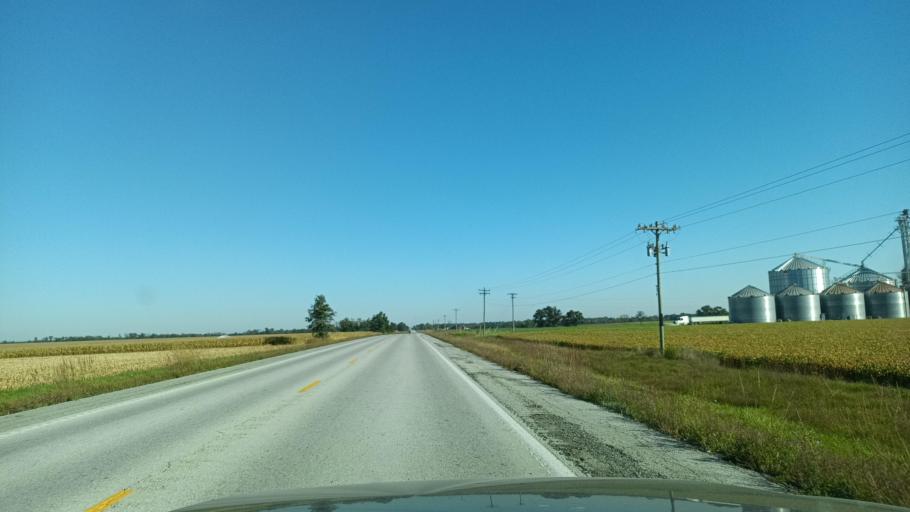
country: US
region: Missouri
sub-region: Audrain County
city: Vandalia
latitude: 39.3662
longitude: -91.6423
